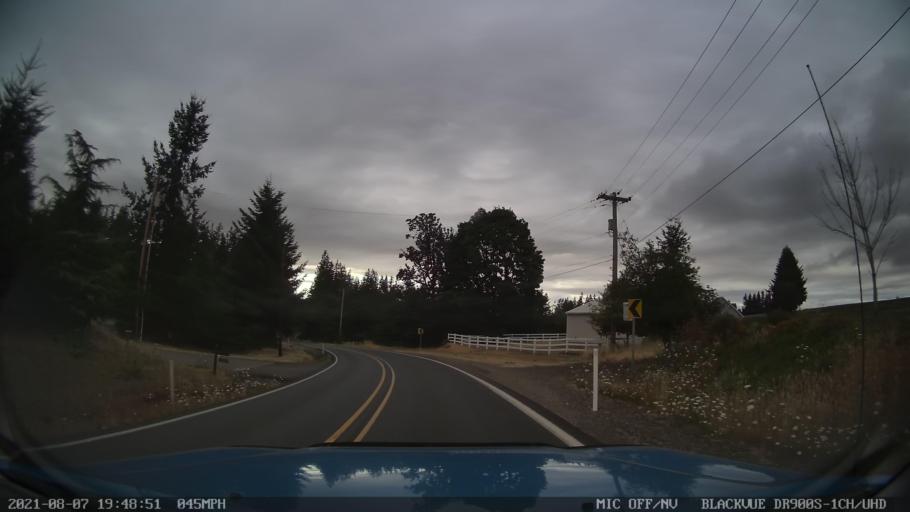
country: US
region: Oregon
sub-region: Marion County
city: Silverton
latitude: 44.9790
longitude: -122.7184
